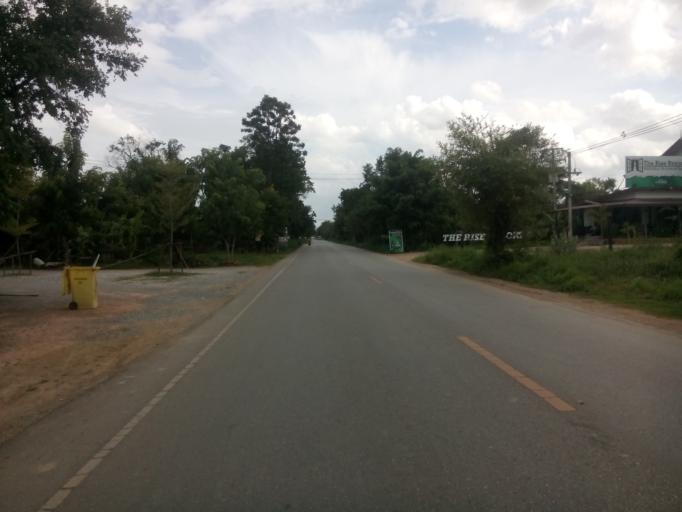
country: TH
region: Sukhothai
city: Ban Na
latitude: 17.0144
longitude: 99.7147
